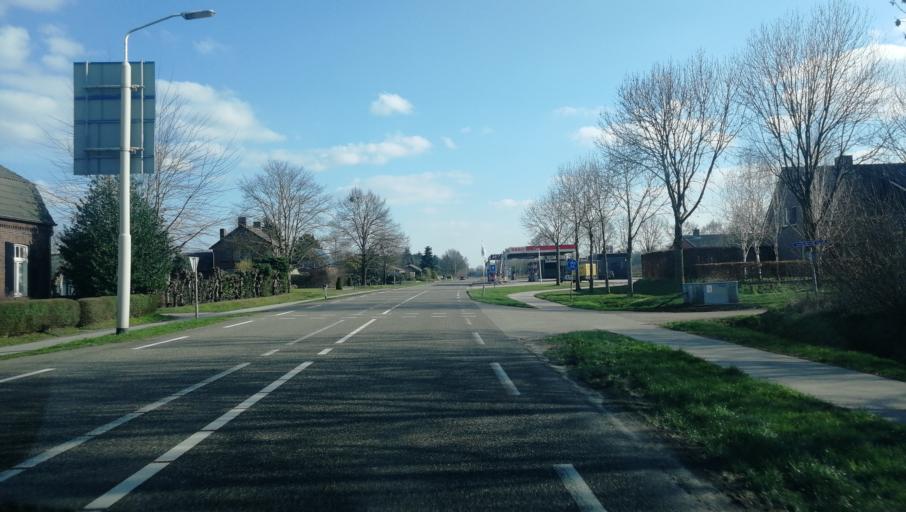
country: NL
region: Limburg
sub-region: Gemeente Peel en Maas
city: Maasbree
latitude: 51.4117
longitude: 6.0480
